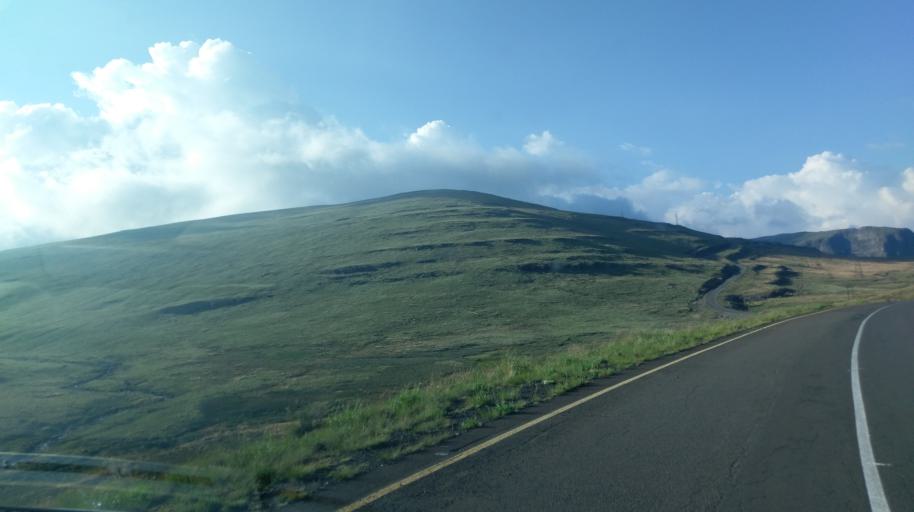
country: LS
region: Butha-Buthe
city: Butha-Buthe
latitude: -29.0837
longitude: 28.4255
